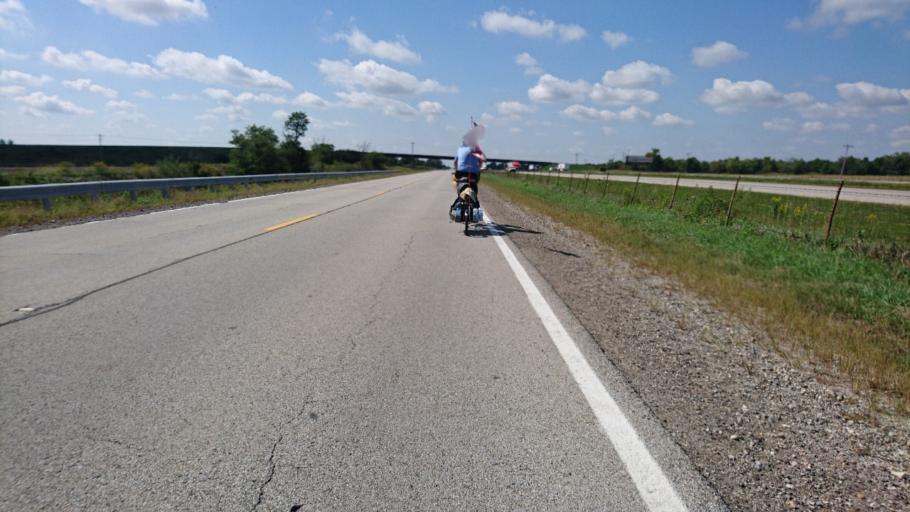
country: US
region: Illinois
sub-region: McLean County
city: Lexington
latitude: 40.6061
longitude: -88.8369
